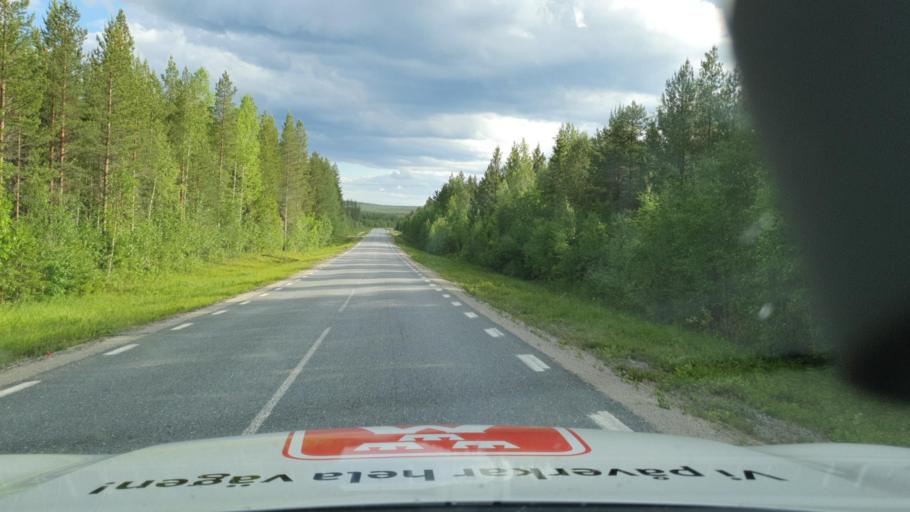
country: SE
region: Vaesterbotten
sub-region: Vindelns Kommun
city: Vindeln
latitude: 64.4299
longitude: 19.7034
